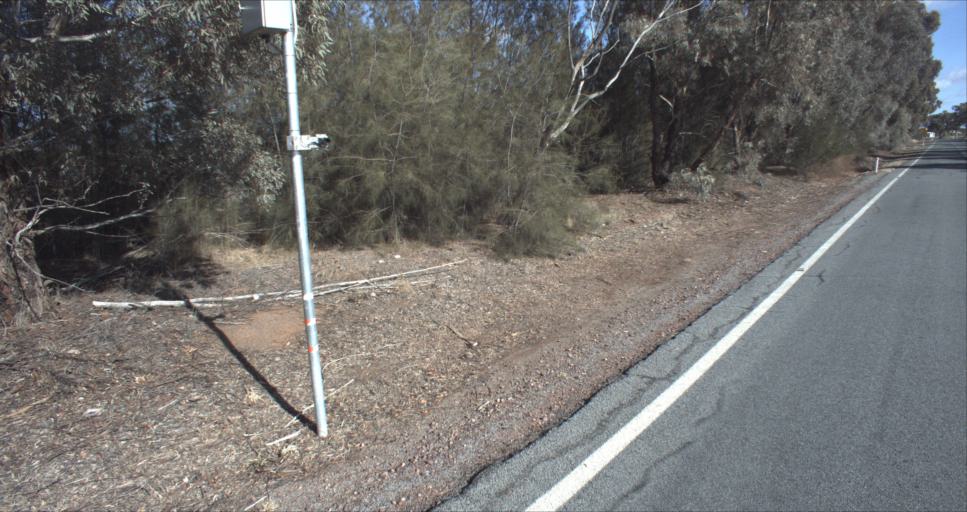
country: AU
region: New South Wales
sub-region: Leeton
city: Leeton
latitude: -34.5481
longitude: 146.3551
